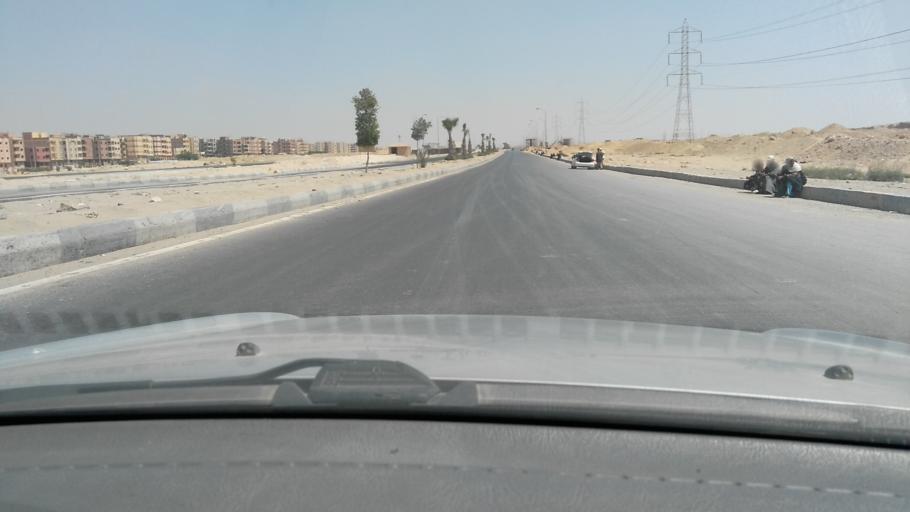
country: EG
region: Al Jizah
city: Madinat Sittah Uktubar
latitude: 29.9300
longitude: 30.9426
